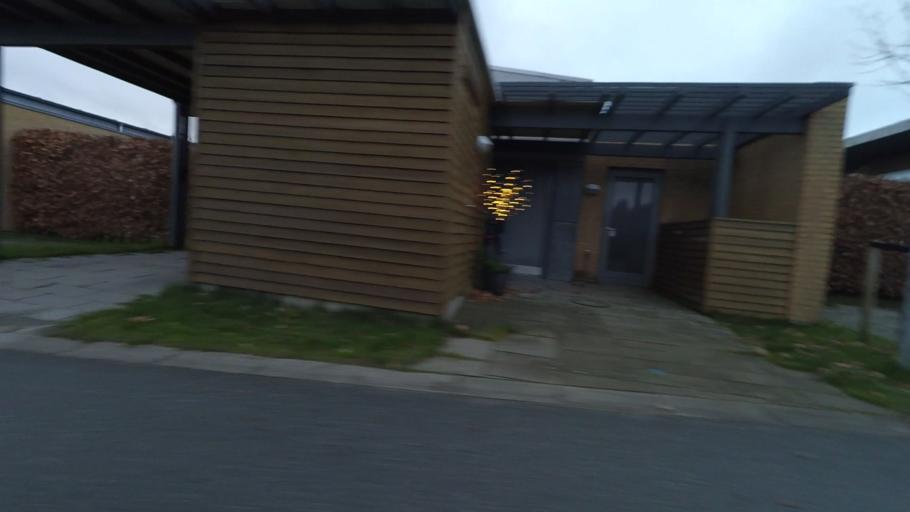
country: DK
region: Central Jutland
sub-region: Arhus Kommune
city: Marslet
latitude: 56.1031
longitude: 10.1757
